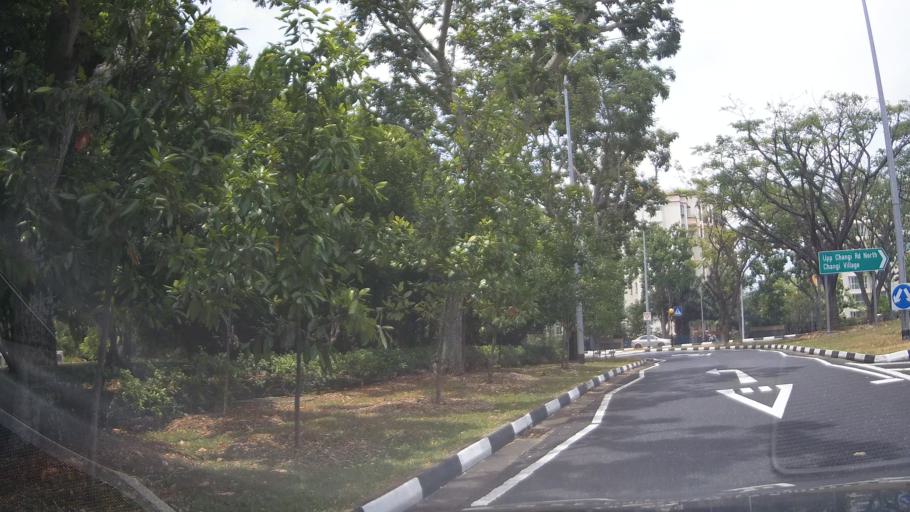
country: SG
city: Singapore
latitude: 1.3483
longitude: 103.9642
